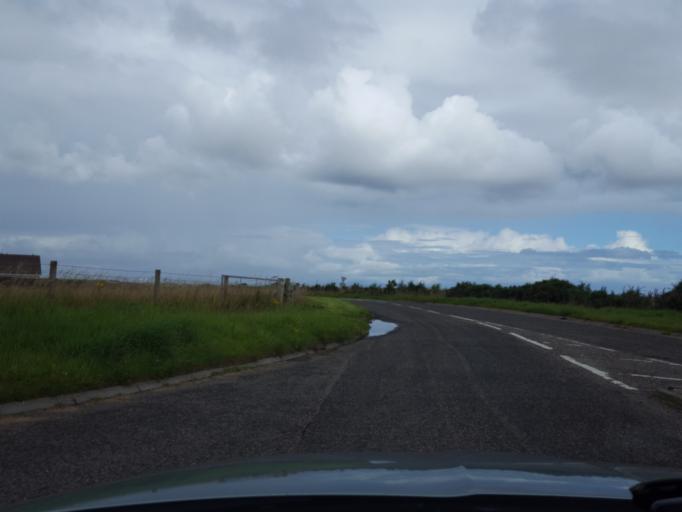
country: GB
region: Scotland
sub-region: Moray
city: Kinloss
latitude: 57.6240
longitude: -3.5372
